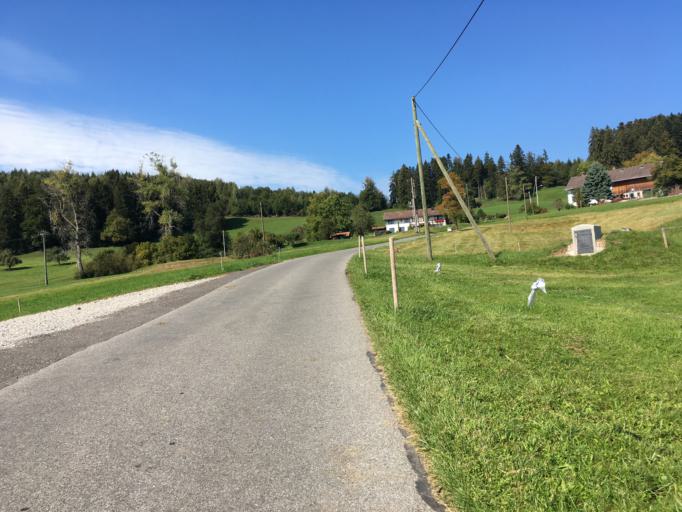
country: CH
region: Zurich
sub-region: Bezirk Hinwil
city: Baretswil
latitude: 47.3427
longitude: 8.8431
